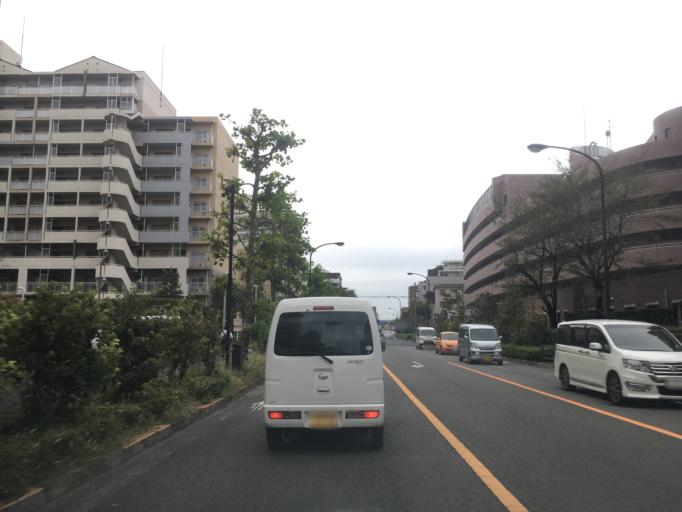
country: JP
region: Tokyo
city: Kokubunji
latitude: 35.6984
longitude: 139.4668
